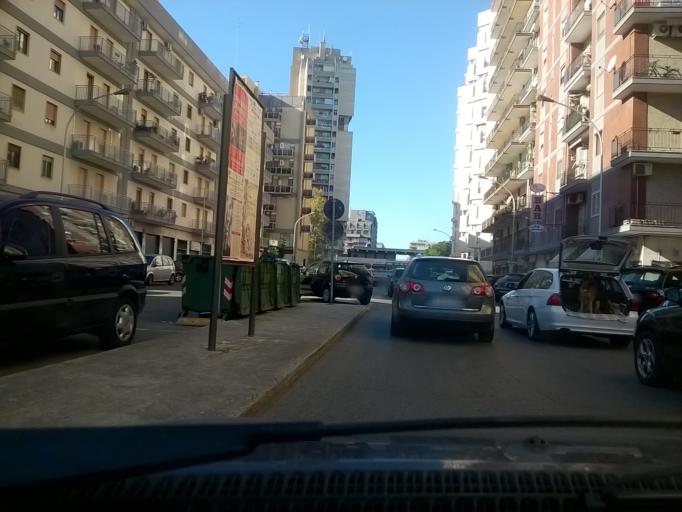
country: IT
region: Apulia
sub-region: Provincia di Taranto
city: Taranto
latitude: 40.4631
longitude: 17.2638
